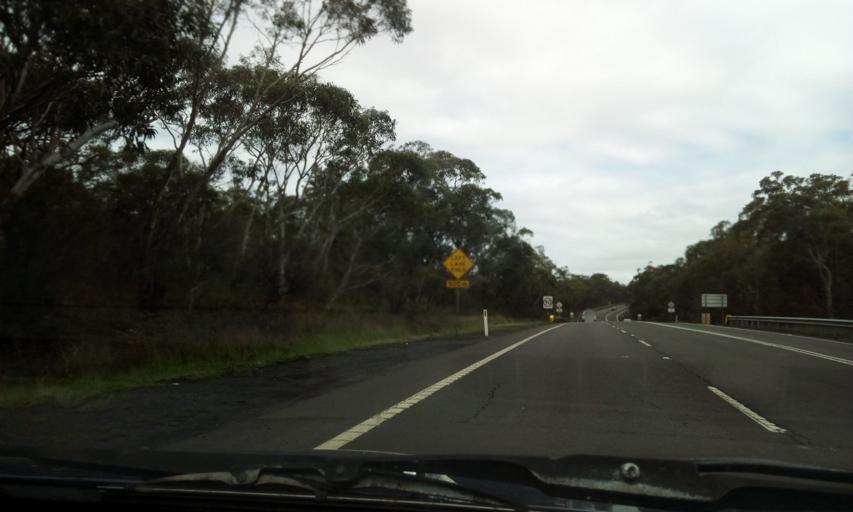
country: AU
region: New South Wales
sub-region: Wollondilly
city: Douglas Park
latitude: -34.2232
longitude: 150.8115
